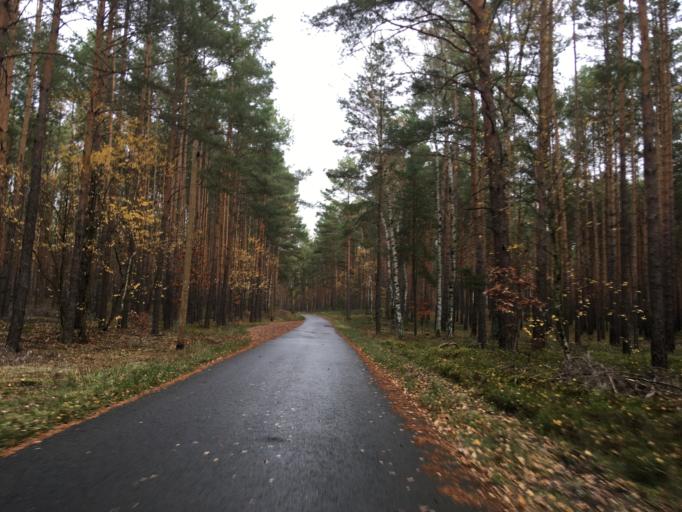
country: DE
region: Brandenburg
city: Tauer
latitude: 51.9156
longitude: 14.4670
